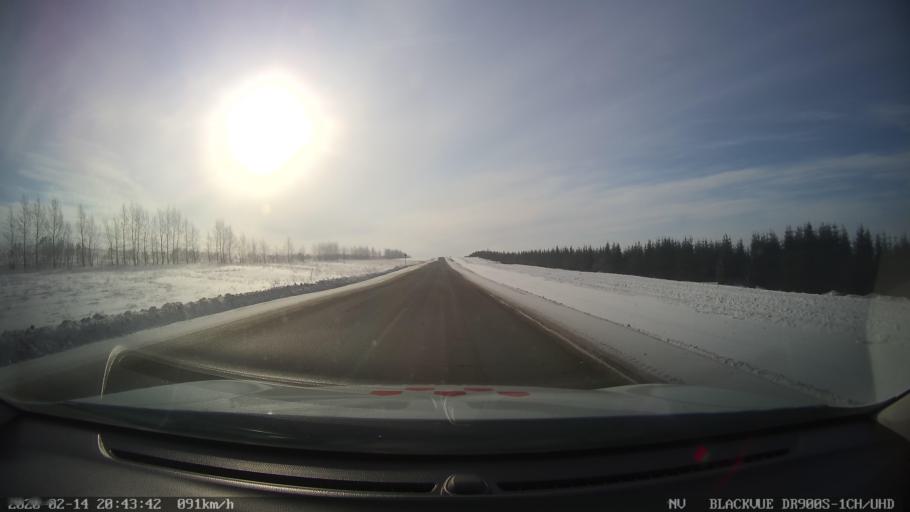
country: RU
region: Tatarstan
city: Kuybyshevskiy Zaton
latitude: 55.3045
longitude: 49.1482
